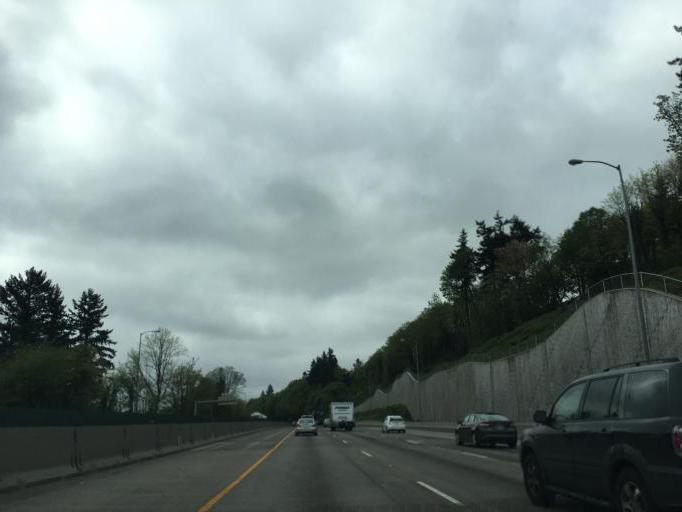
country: US
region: Oregon
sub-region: Multnomah County
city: Portland
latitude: 45.4797
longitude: -122.6790
